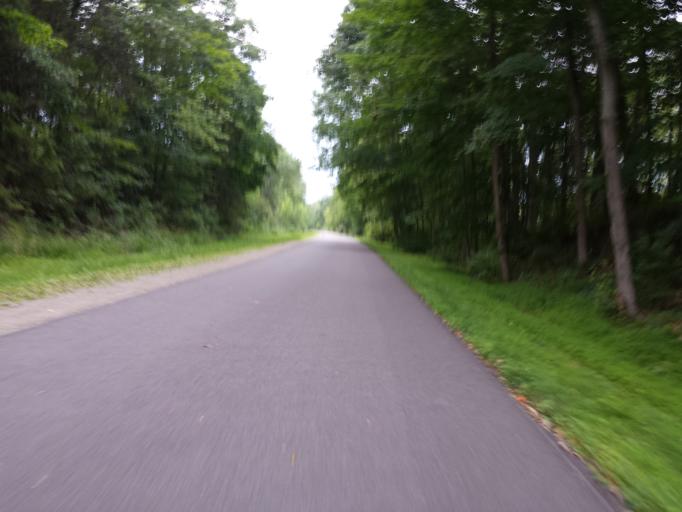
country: US
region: New York
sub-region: Dutchess County
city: Red Oaks Mill
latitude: 41.6652
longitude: -73.8545
